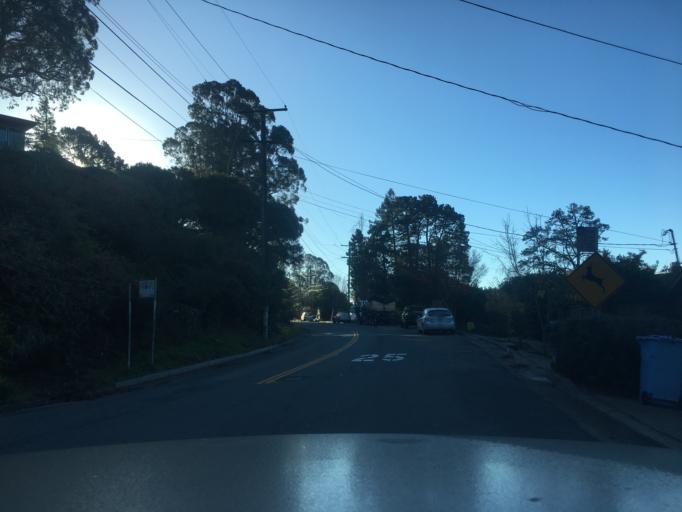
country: US
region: California
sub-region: Contra Costa County
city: Kensington
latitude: 37.8964
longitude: -122.2606
